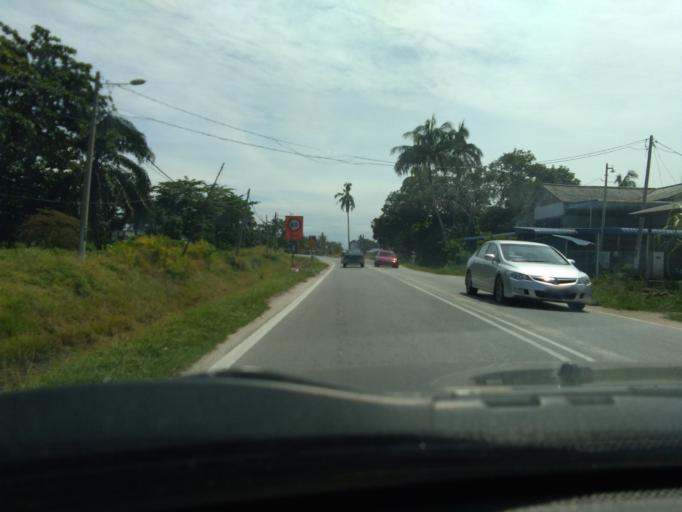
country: MY
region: Perak
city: Bagan Serai
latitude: 5.0134
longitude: 100.5379
